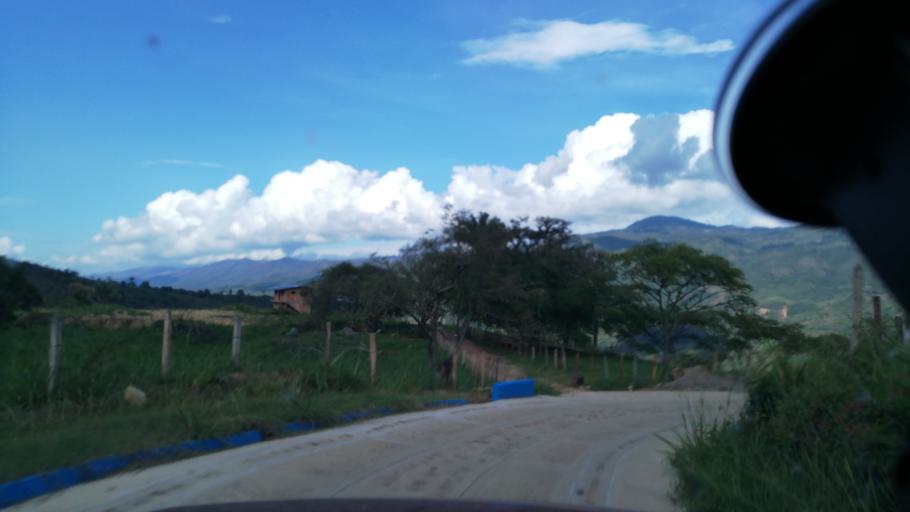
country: CO
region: Cundinamarca
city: Quipile
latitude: 4.7741
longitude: -74.6164
